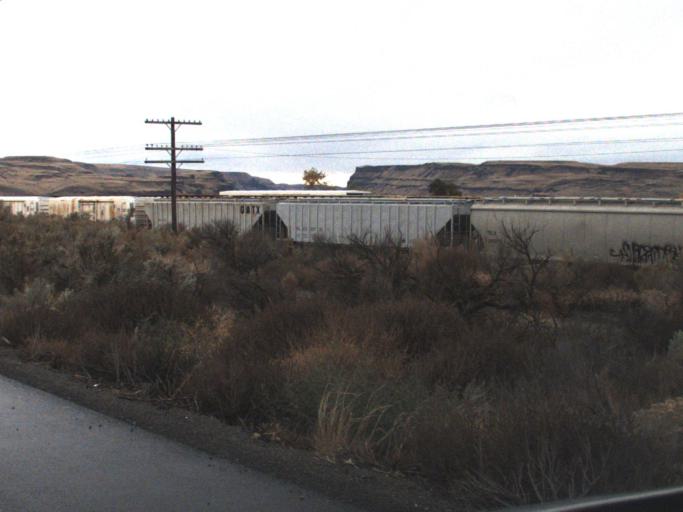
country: US
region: Washington
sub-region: Benton County
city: Finley
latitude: 46.0907
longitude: -118.9110
